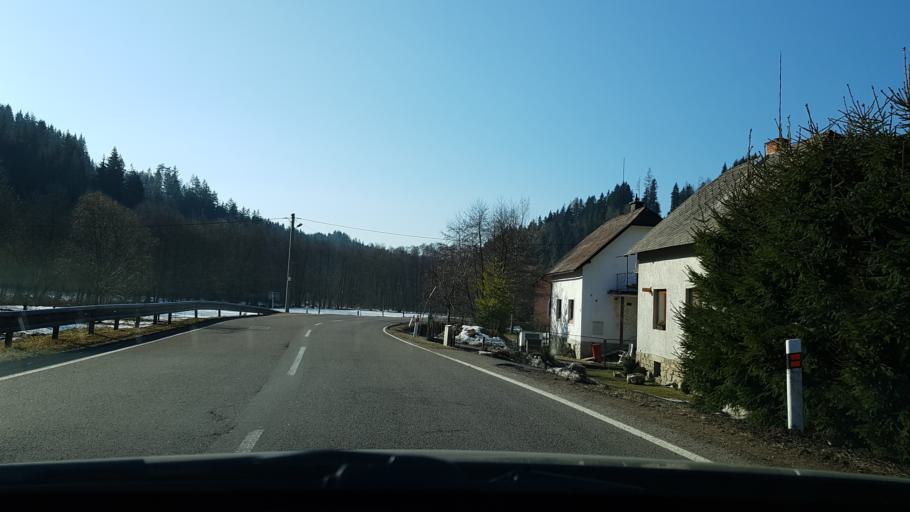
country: CZ
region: Olomoucky
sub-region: Okres Sumperk
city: Hanusovice
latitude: 50.0943
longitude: 16.9780
